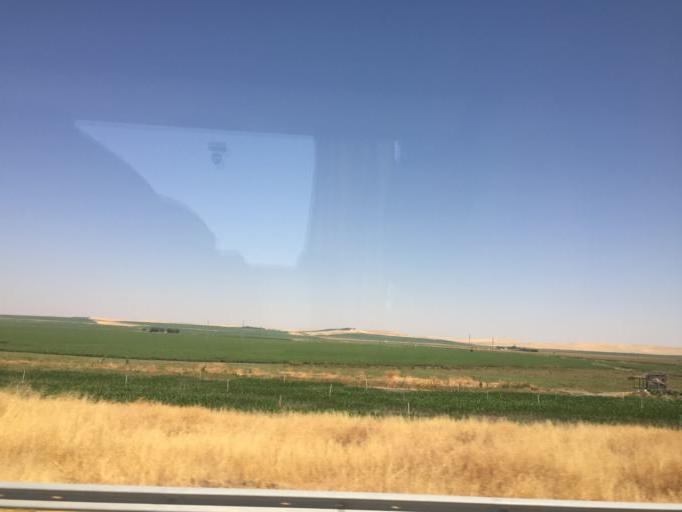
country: TR
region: Diyarbakir
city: Tepe
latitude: 37.8503
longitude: 40.7746
